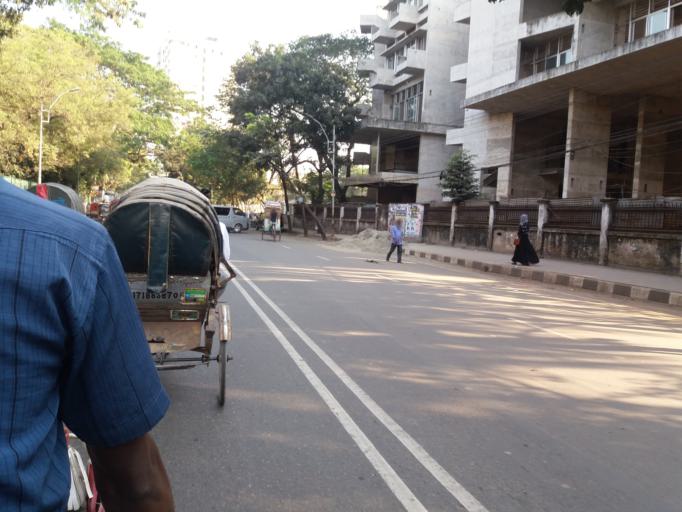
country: BD
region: Dhaka
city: Azimpur
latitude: 23.7250
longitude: 90.3938
